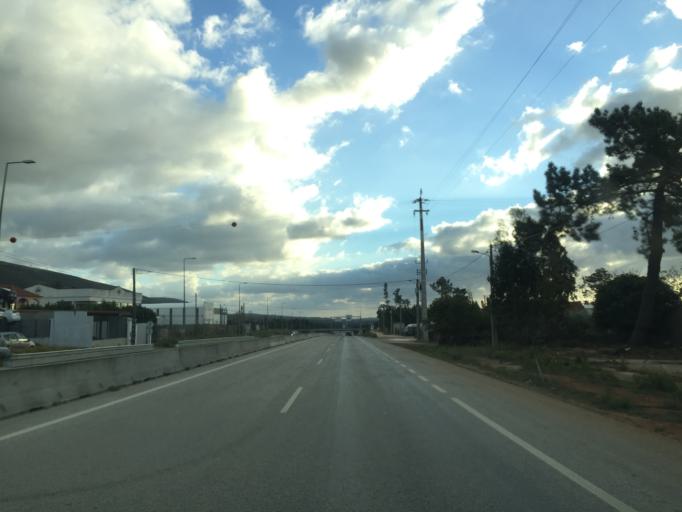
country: PT
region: Leiria
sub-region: Alcobaca
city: Aljubarrota
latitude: 39.5613
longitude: -8.8848
